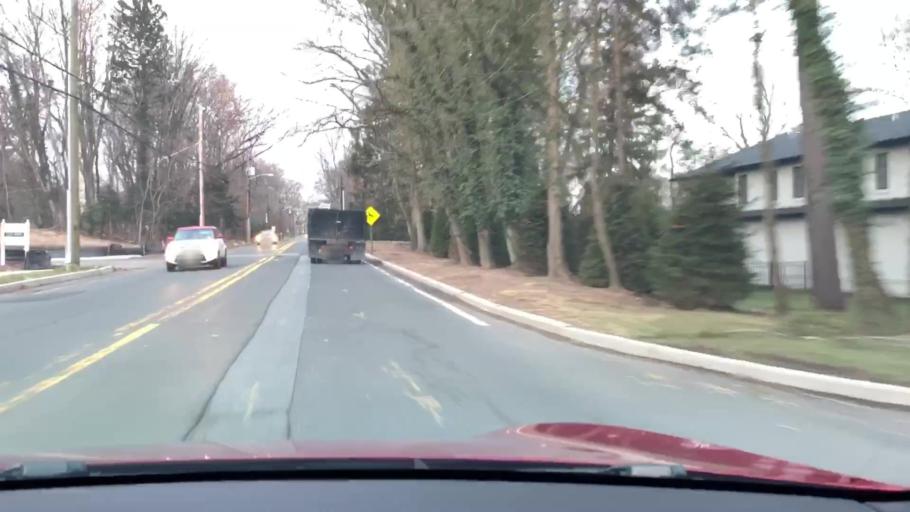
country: US
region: New Jersey
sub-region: Bergen County
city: Tenafly
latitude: 40.9138
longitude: -73.9800
